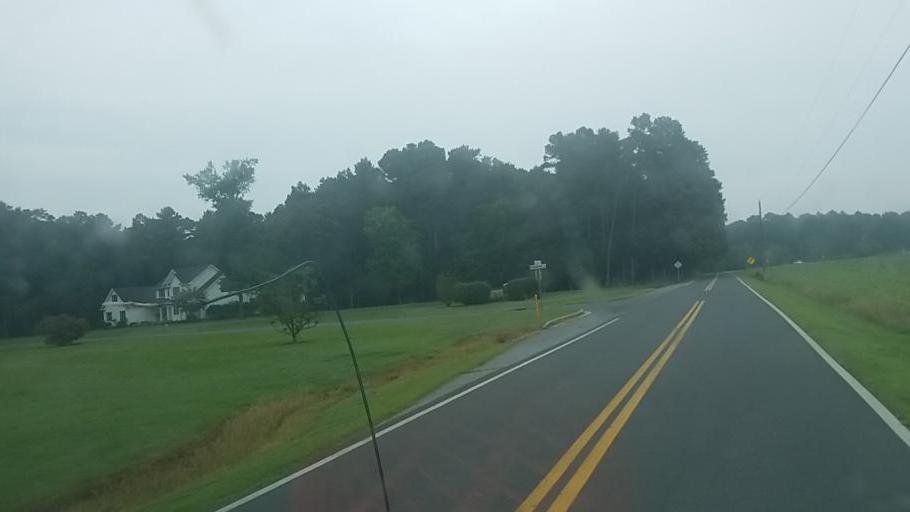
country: US
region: Maryland
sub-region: Wicomico County
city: Delmar
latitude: 38.4030
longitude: -75.5265
